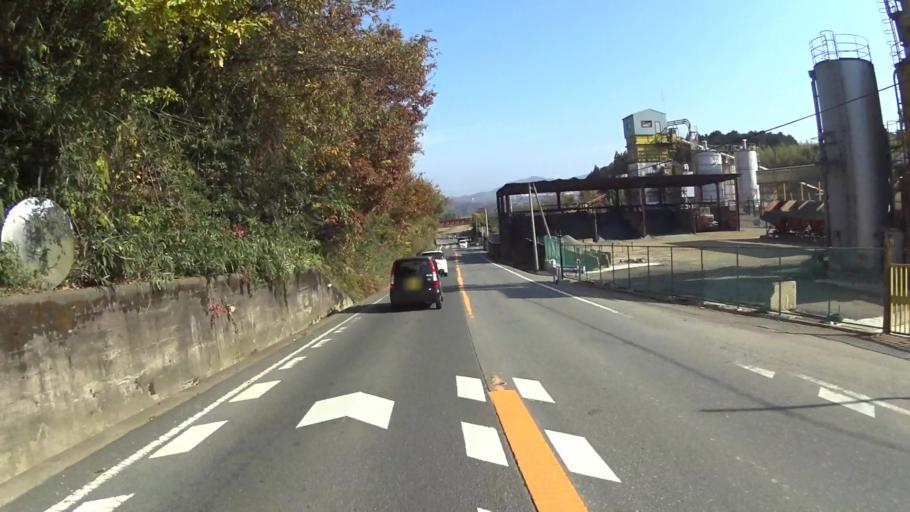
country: JP
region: Kyoto
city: Fukuchiyama
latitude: 35.2688
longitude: 135.1448
